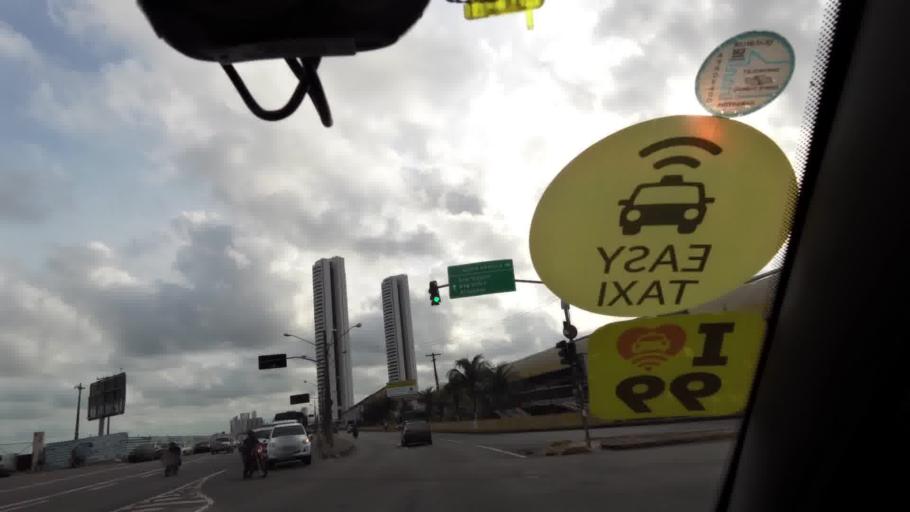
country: BR
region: Pernambuco
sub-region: Recife
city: Recife
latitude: -8.0679
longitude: -34.8751
